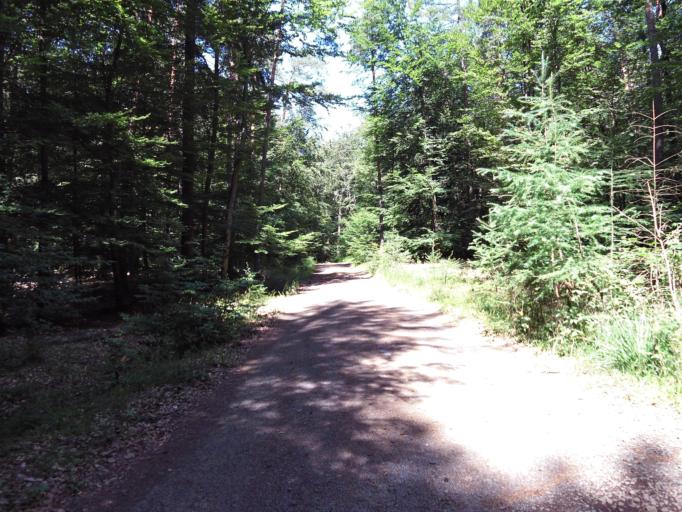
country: DE
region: Rheinland-Pfalz
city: Carlsberg
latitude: 49.4752
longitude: 8.0177
